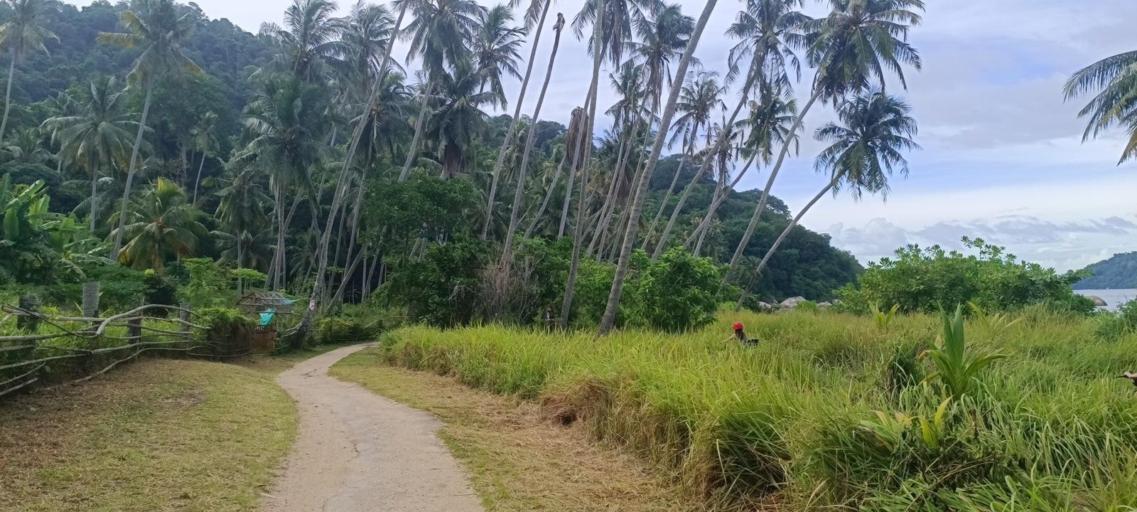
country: MY
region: Penang
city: Kampung Sungai Ara
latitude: 5.2668
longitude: 100.2719
